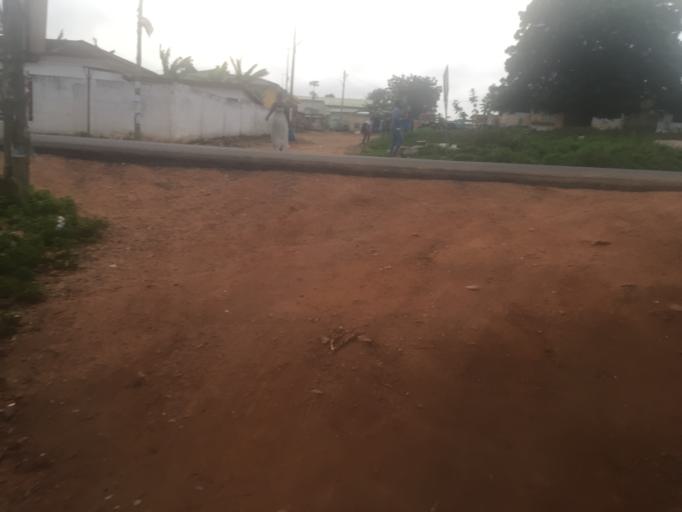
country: GH
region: Greater Accra
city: Dome
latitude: 5.6041
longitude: -0.2239
